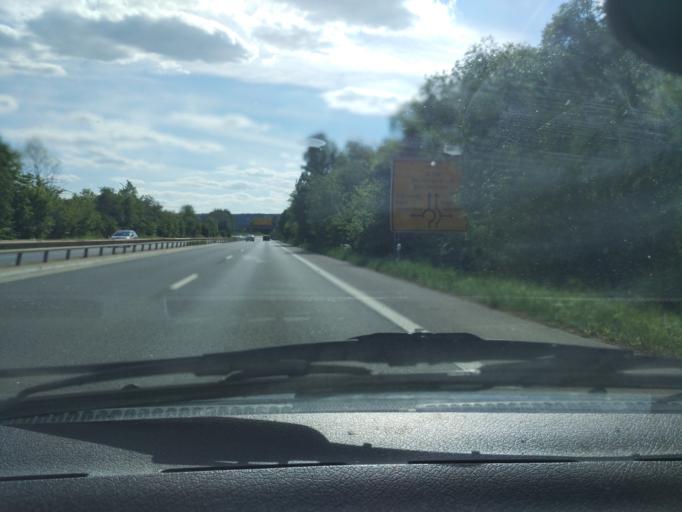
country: DE
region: Rheinland-Pfalz
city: Munster-Sarmsheim
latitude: 49.9466
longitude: 7.9243
